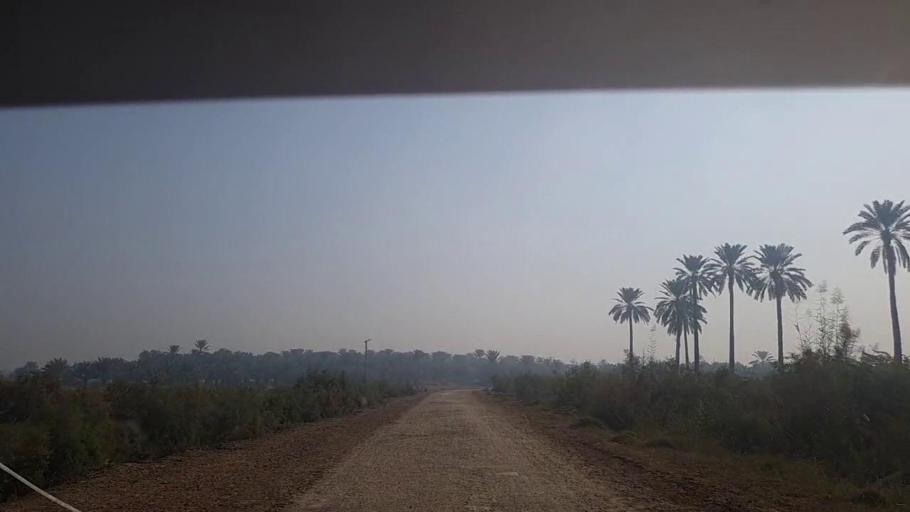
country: PK
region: Sindh
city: Khairpur
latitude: 27.4797
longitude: 68.7175
